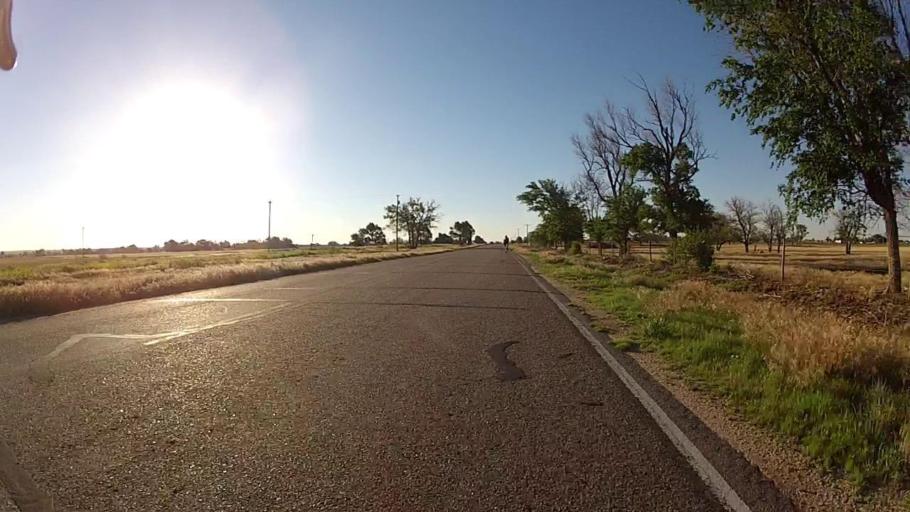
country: US
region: Kansas
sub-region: Ford County
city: Dodge City
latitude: 37.7106
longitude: -99.9183
